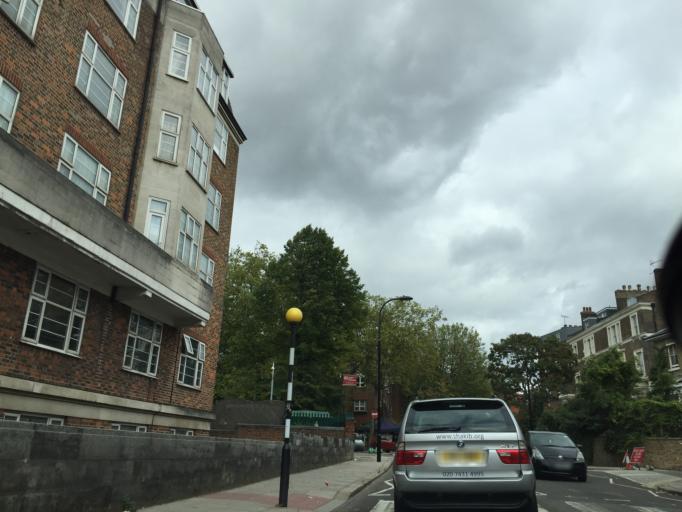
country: GB
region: England
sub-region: Greater London
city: Belsize Park
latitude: 51.5447
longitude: -0.1751
